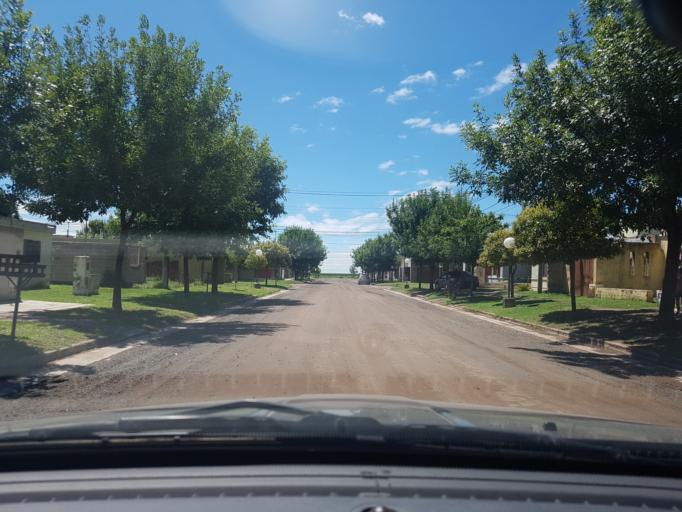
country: AR
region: Cordoba
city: Las Perdices
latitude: -32.7580
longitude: -63.7749
